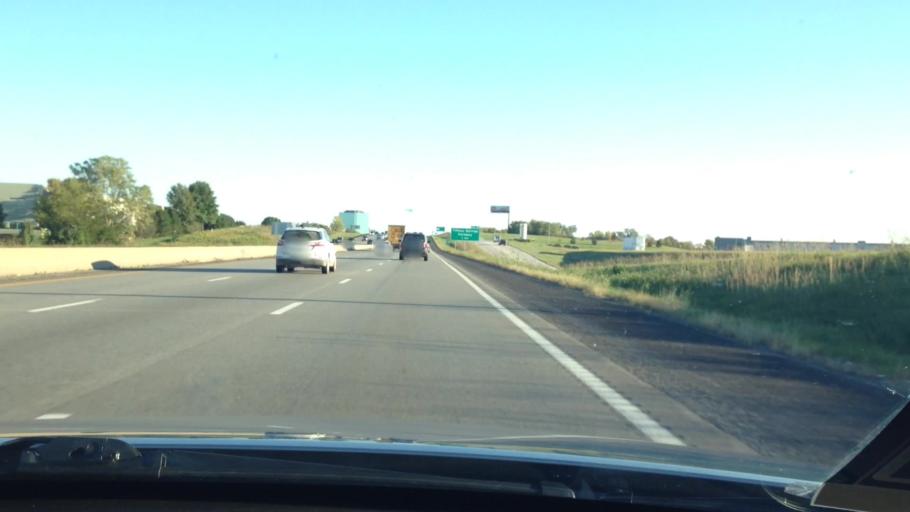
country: US
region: Missouri
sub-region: Platte County
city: Weatherby Lake
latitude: 39.2895
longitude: -94.6814
